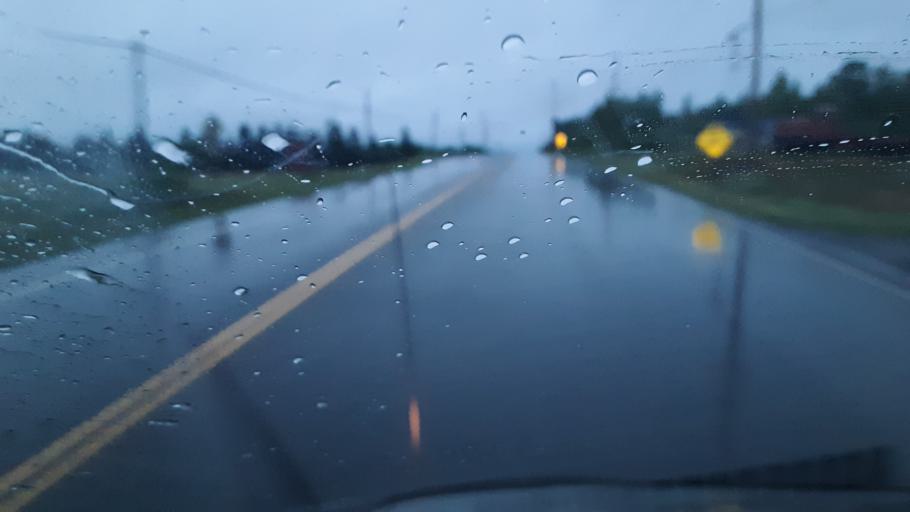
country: US
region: Maine
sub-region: Penobscot County
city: Patten
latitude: 45.9820
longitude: -68.4500
